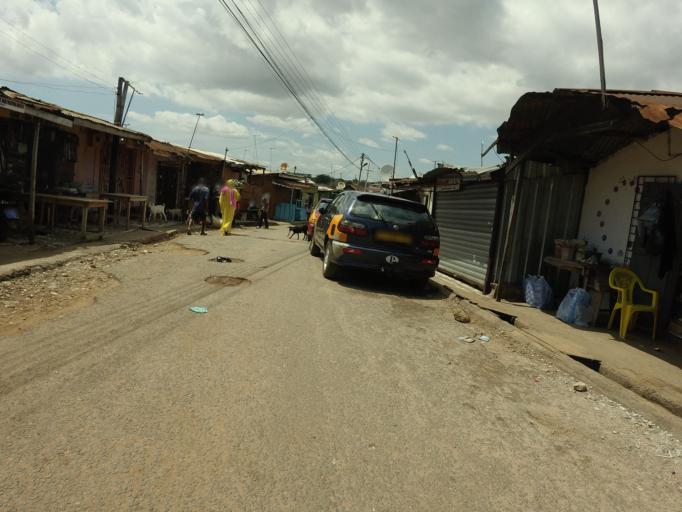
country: GH
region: Greater Accra
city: Accra
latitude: 5.5842
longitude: -0.2006
